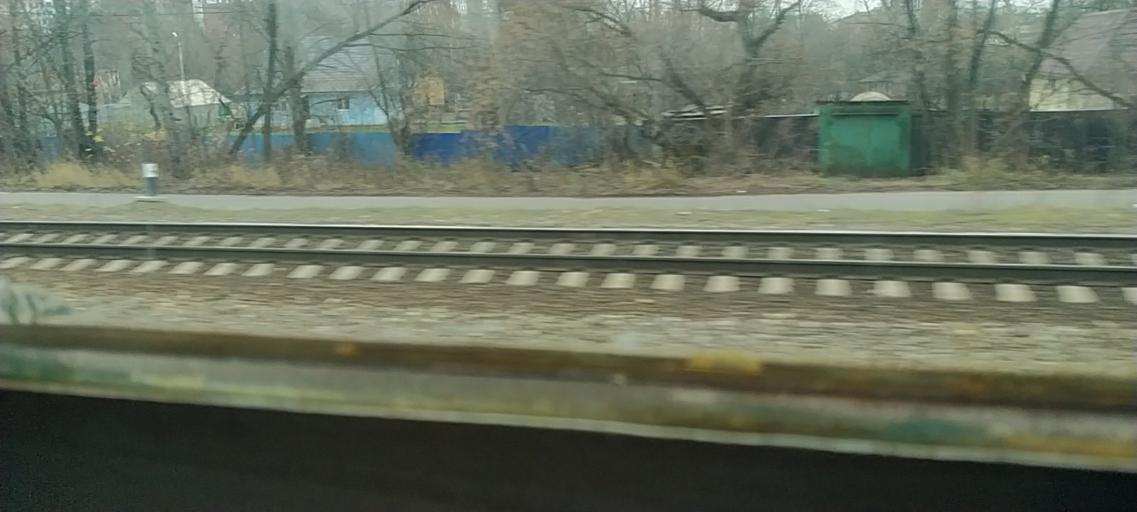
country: RU
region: Moskovskaya
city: Korenevo
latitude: 55.6686
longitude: 37.9969
